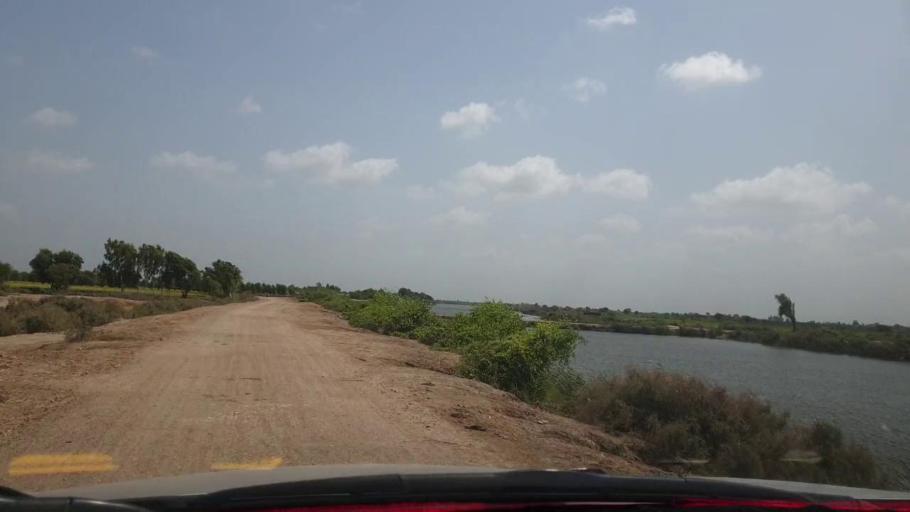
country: PK
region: Sindh
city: Talhar
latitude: 24.8763
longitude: 68.9116
